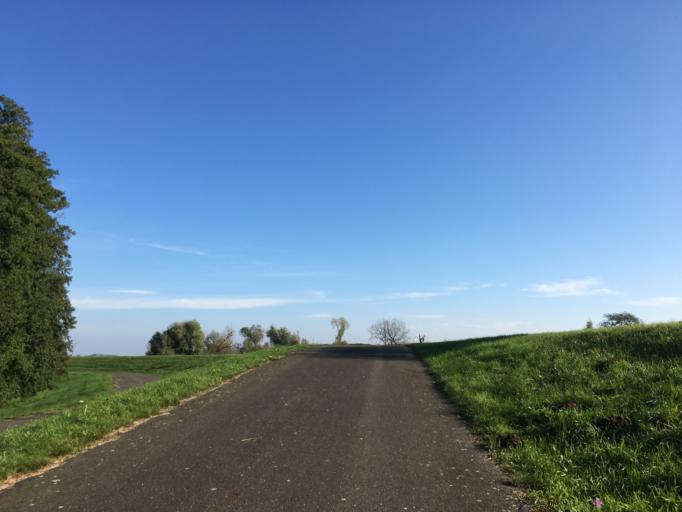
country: DE
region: Brandenburg
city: Reitwein
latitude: 52.5222
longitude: 14.6033
